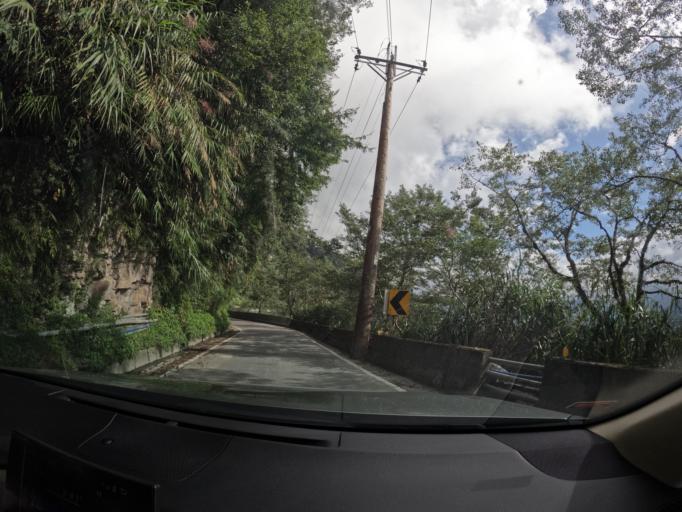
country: TW
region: Taiwan
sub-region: Taitung
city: Taitung
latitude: 23.2378
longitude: 121.0044
